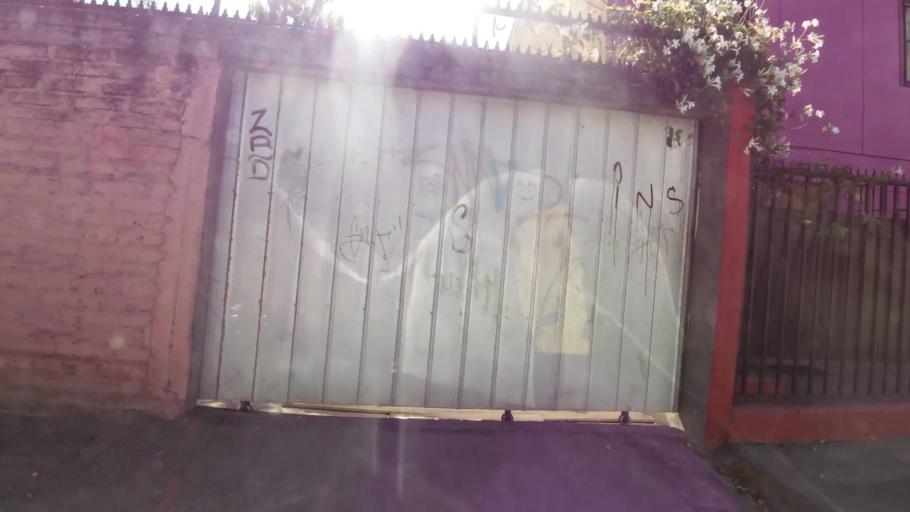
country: CL
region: O'Higgins
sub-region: Provincia de Colchagua
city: Chimbarongo
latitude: -34.5775
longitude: -71.0018
